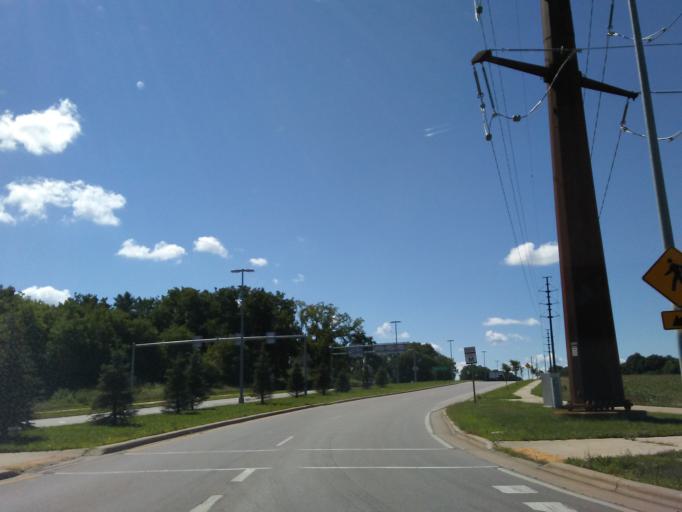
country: US
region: Wisconsin
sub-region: Dane County
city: Verona
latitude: 43.0458
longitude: -89.5330
